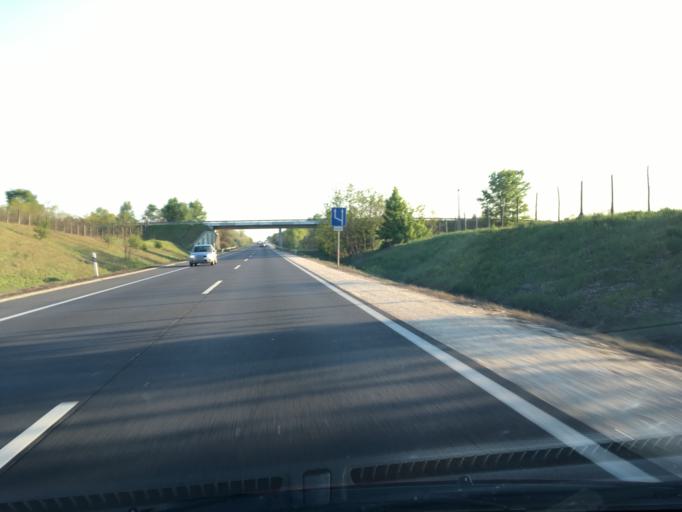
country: HU
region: Pest
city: God
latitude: 47.6687
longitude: 19.1664
